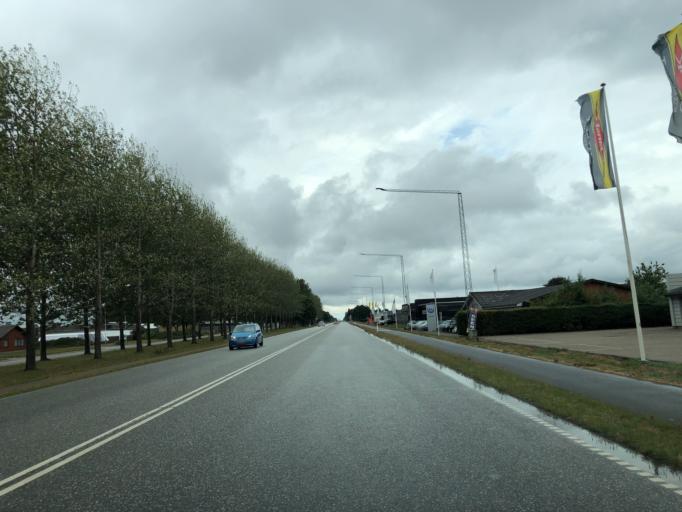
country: DK
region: Central Jutland
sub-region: Ikast-Brande Kommune
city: Ikast
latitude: 56.1380
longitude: 9.1371
